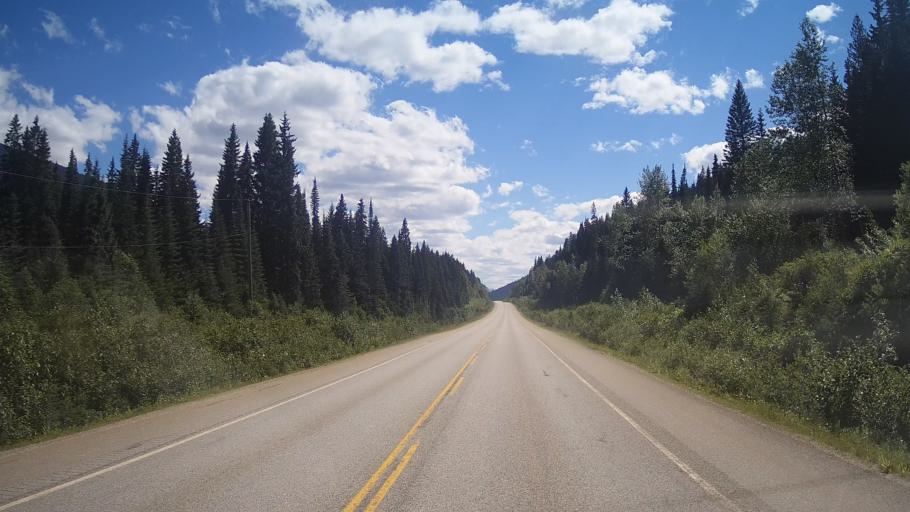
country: CA
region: Alberta
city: Jasper Park Lodge
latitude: 52.5601
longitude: -119.1098
